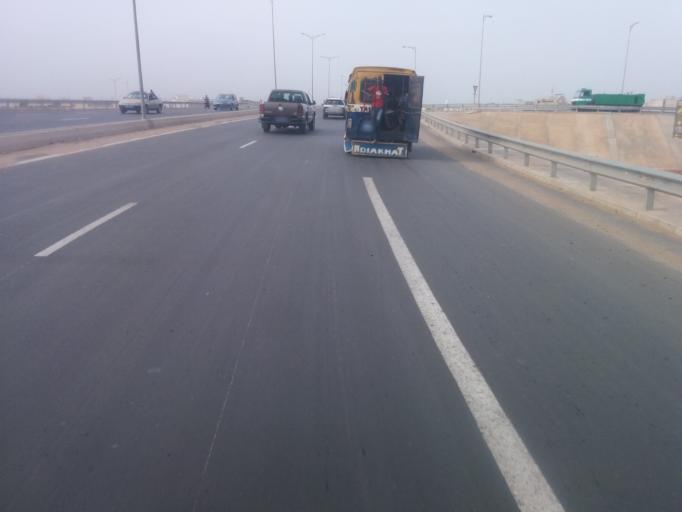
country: SN
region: Dakar
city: Grand Dakar
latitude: 14.7449
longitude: -17.4468
